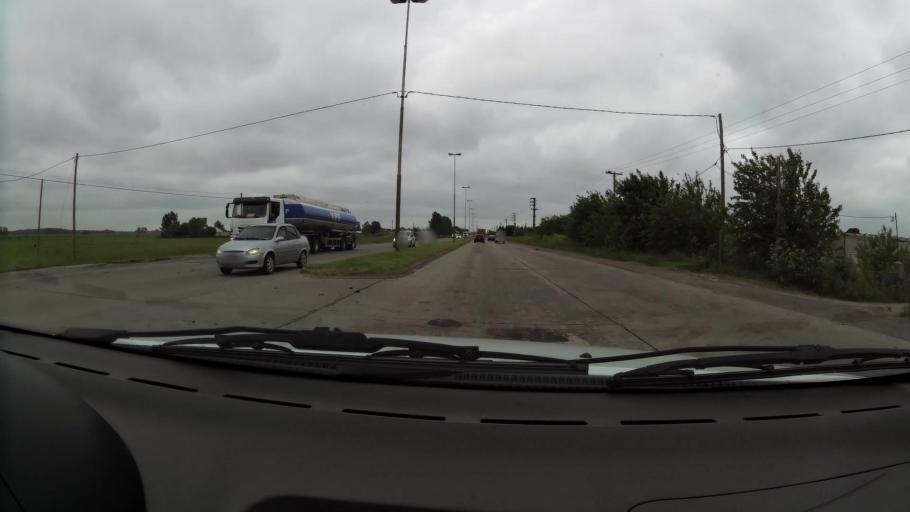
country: AR
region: Buenos Aires
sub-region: Partido de Brandsen
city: Brandsen
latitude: -35.0460
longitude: -58.1037
